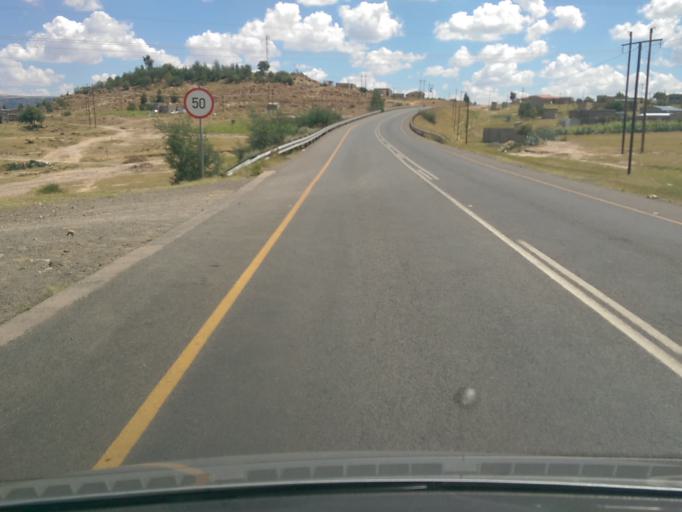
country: LS
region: Maseru
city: Maseru
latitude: -29.3958
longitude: 27.5238
